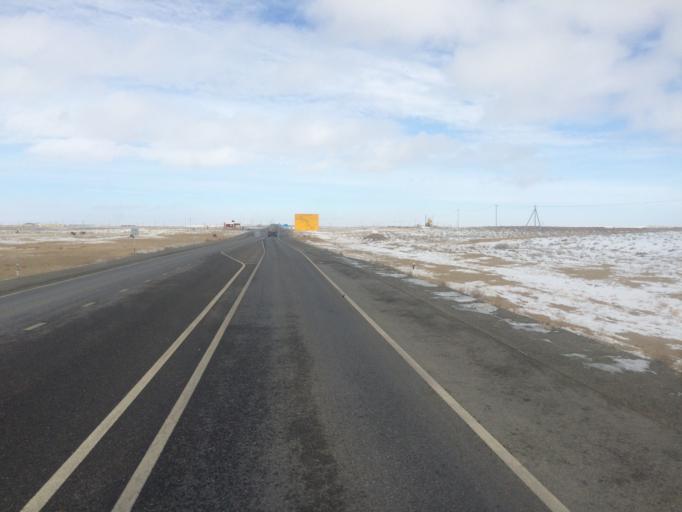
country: KZ
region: Qyzylorda
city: Aral
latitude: 46.7942
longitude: 61.7146
